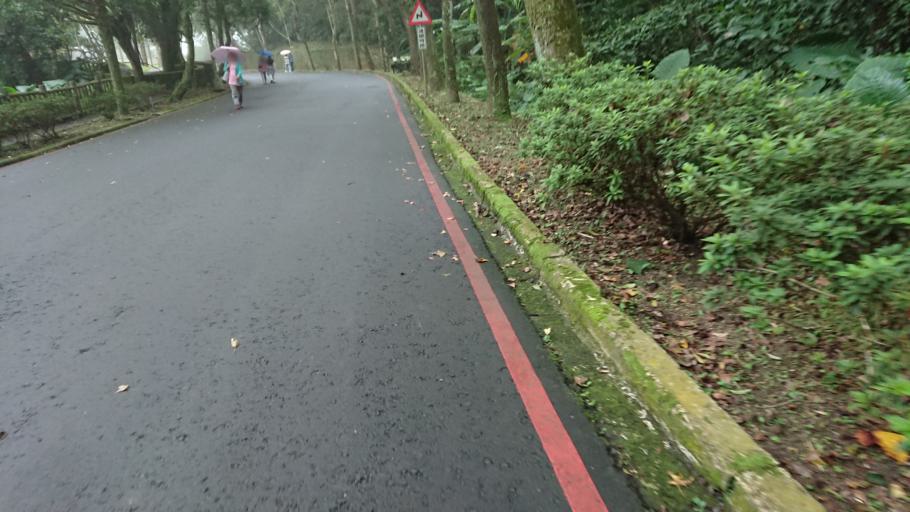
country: TW
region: Taiwan
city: Daxi
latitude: 24.8167
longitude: 121.2409
